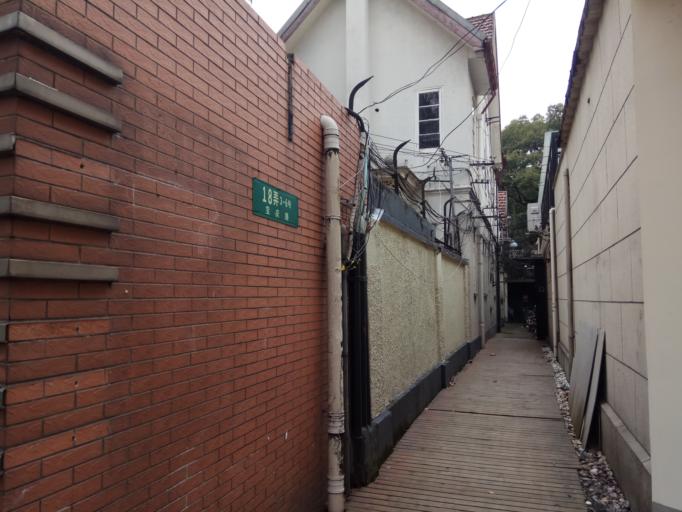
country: CN
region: Shanghai Shi
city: Shanghai
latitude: 31.2122
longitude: 121.4454
